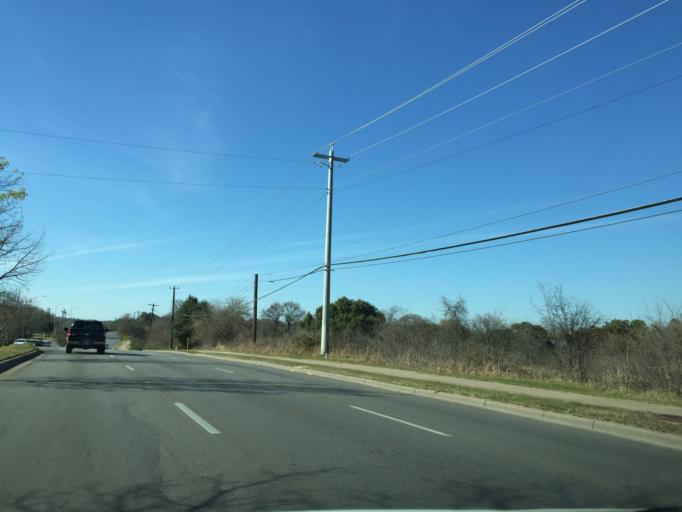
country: US
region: Texas
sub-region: Travis County
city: Austin
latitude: 30.2281
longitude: -97.7099
